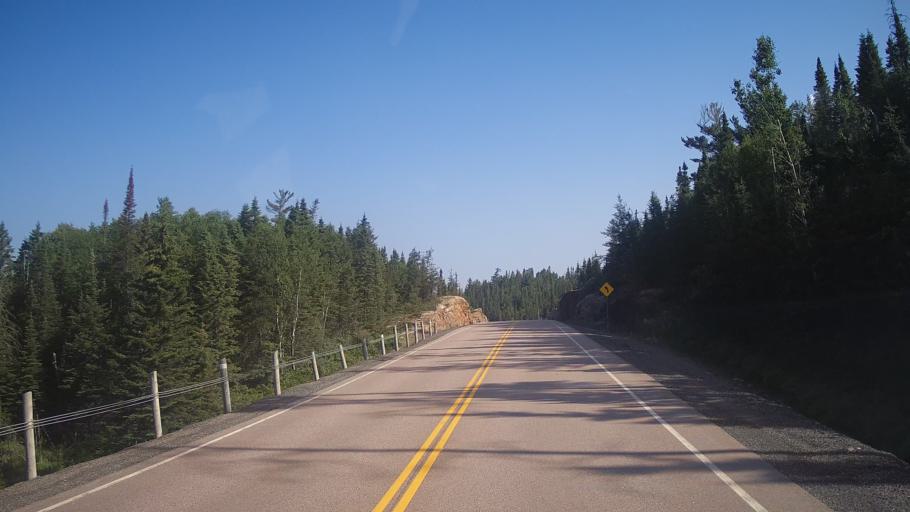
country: CA
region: Ontario
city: Rayside-Balfour
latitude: 47.0104
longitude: -81.6336
